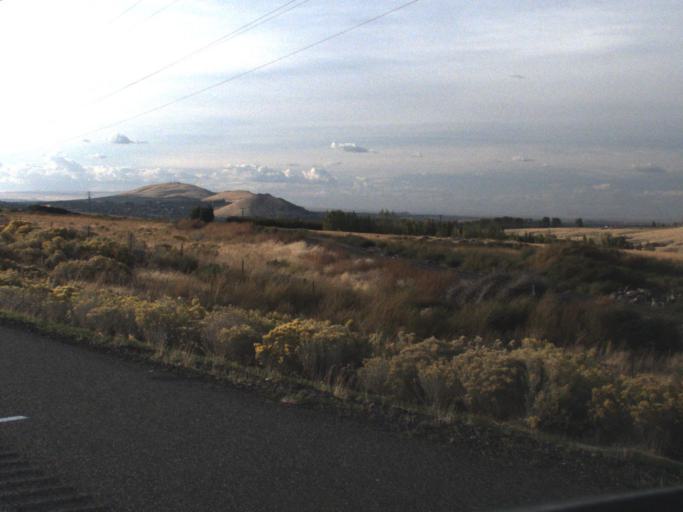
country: US
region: Washington
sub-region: Franklin County
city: West Pasco
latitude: 46.1746
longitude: -119.2178
